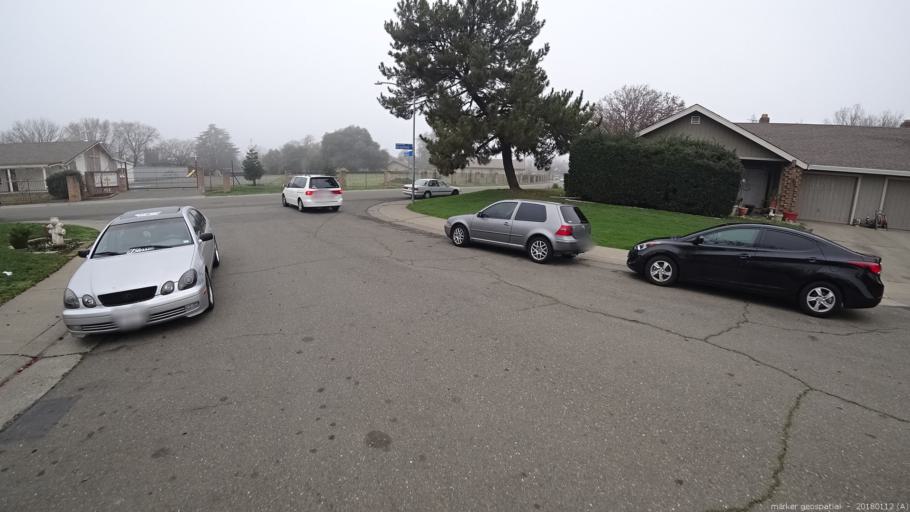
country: US
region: California
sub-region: Sacramento County
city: Gold River
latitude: 38.6082
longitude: -121.2741
